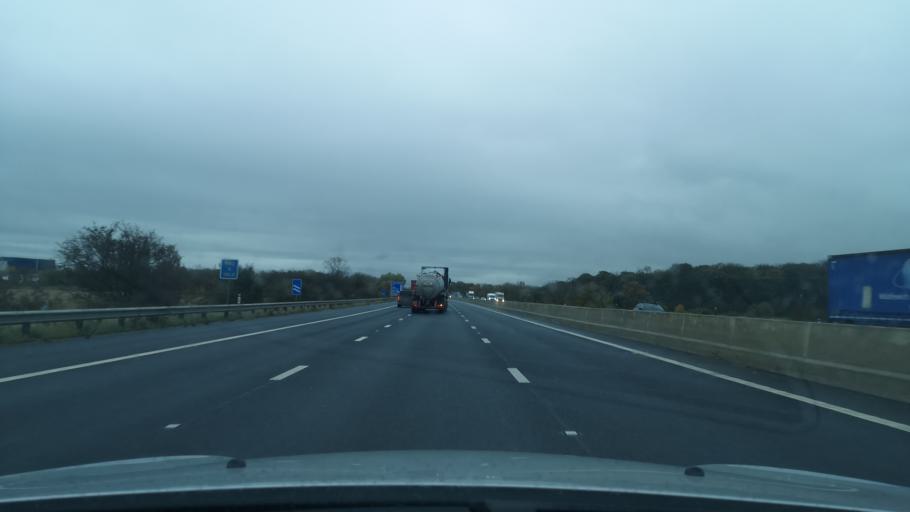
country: GB
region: England
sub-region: Doncaster
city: Norton
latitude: 53.6943
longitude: -1.1668
